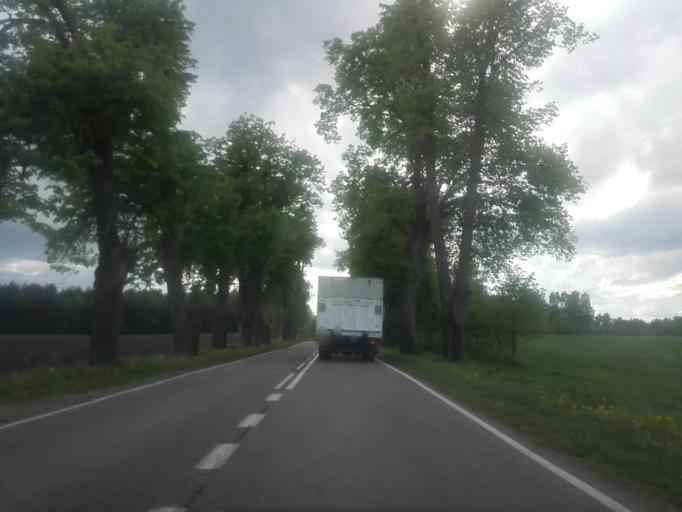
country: PL
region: Podlasie
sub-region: Powiat lomzynski
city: Wizna
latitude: 53.1937
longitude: 22.3028
